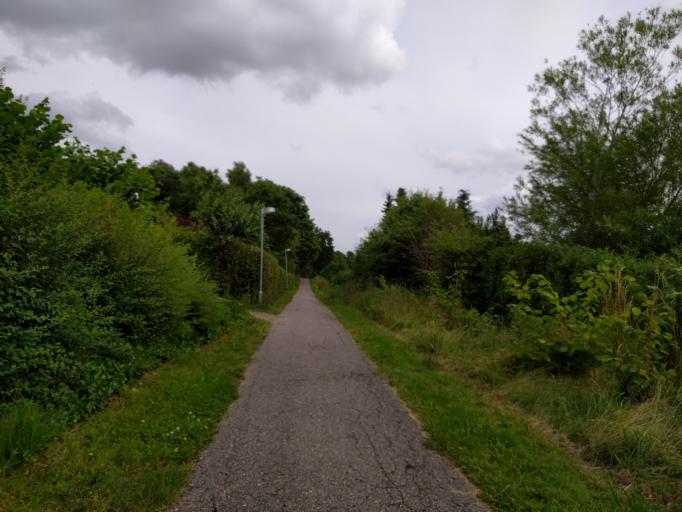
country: DK
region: Central Jutland
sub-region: Skanderborg Kommune
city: Ry
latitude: 56.0840
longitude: 9.7726
